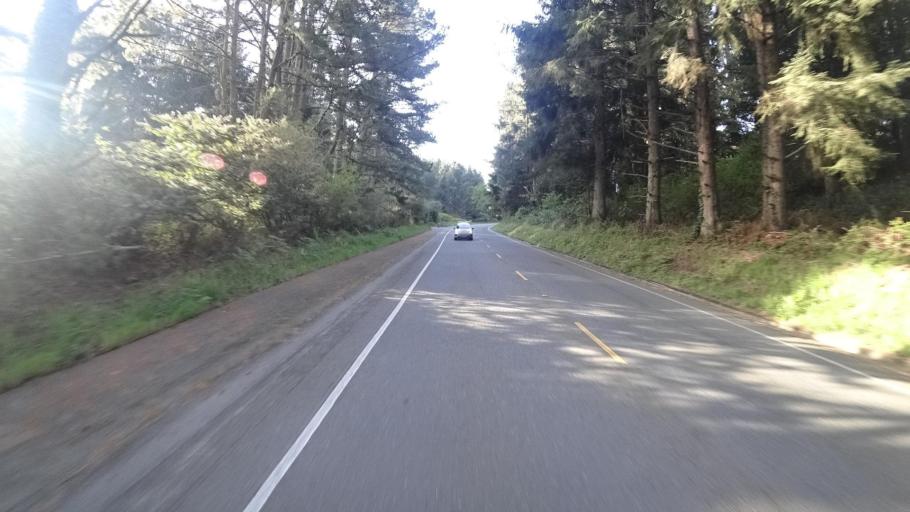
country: US
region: California
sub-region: Humboldt County
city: Humboldt Hill
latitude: 40.7252
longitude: -124.2018
